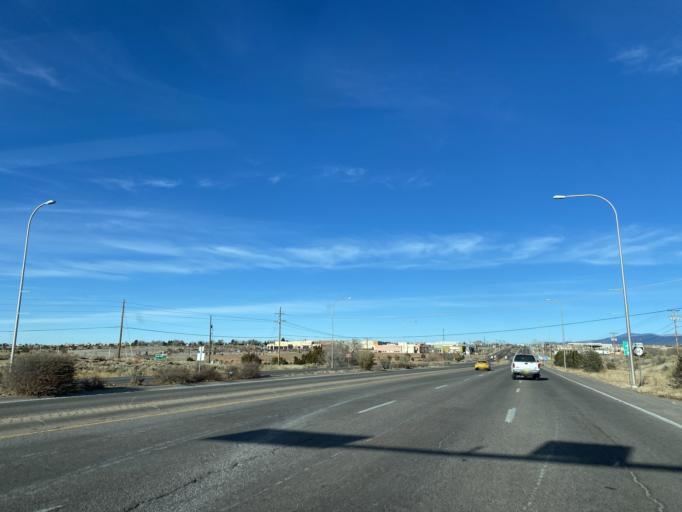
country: US
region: New Mexico
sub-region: Santa Fe County
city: Agua Fria
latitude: 35.6134
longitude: -106.0330
